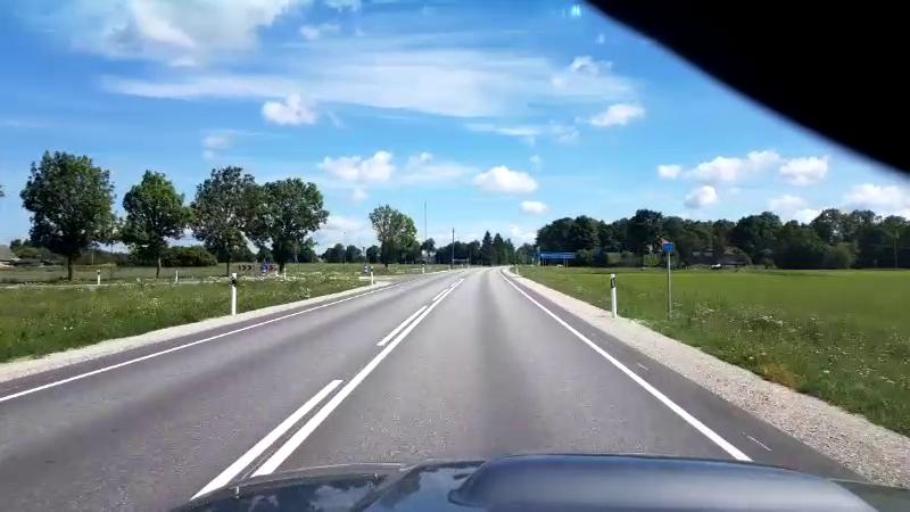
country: EE
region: Jaervamaa
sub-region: Jaerva-Jaani vald
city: Jarva-Jaani
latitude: 59.0948
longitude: 25.6943
